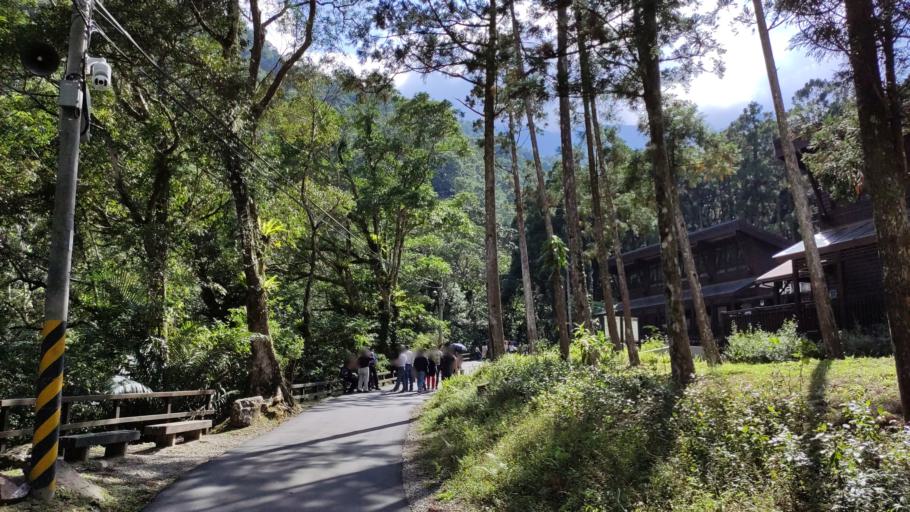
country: TW
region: Taiwan
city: Daxi
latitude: 24.8257
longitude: 121.4486
